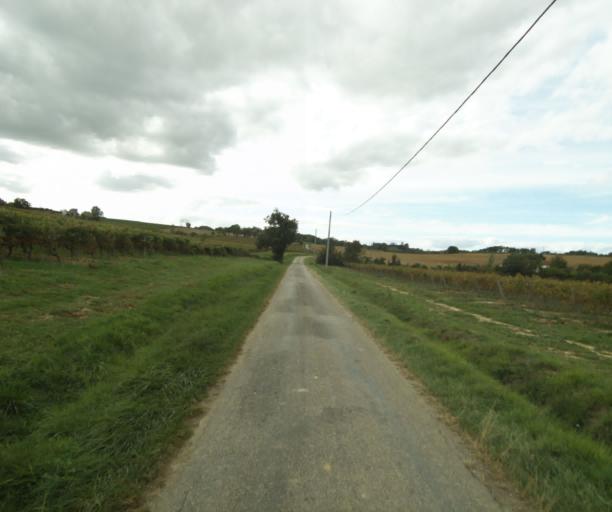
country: FR
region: Midi-Pyrenees
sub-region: Departement du Gers
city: Gondrin
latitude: 43.8611
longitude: 0.2693
